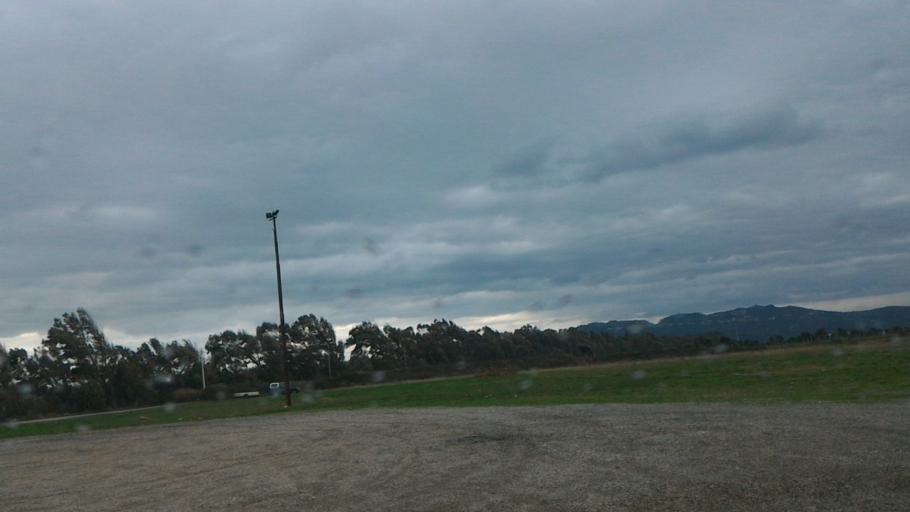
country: IT
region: Calabria
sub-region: Provincia di Crotone
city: Ciro Marina
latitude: 39.4025
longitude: 17.1263
